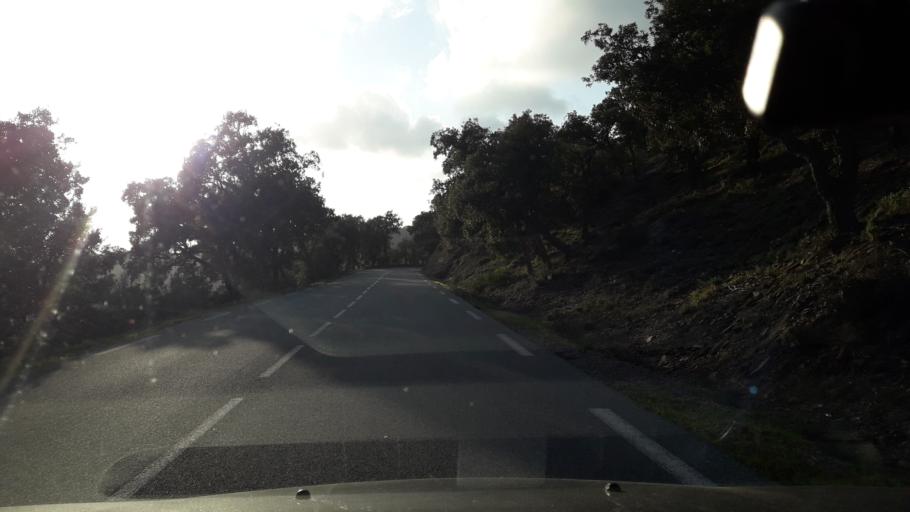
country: FR
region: Provence-Alpes-Cote d'Azur
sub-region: Departement du Var
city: Saint-Raphael
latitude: 43.5013
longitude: 6.7900
